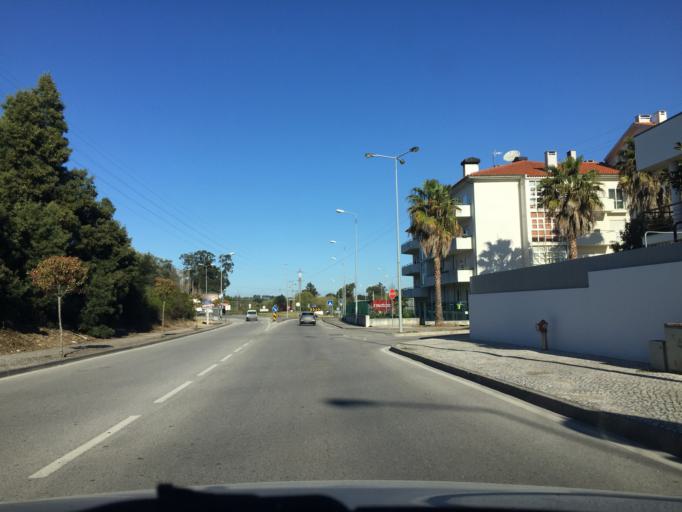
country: PT
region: Aveiro
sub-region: Anadia
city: Arcos
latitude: 40.4430
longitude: -8.4507
